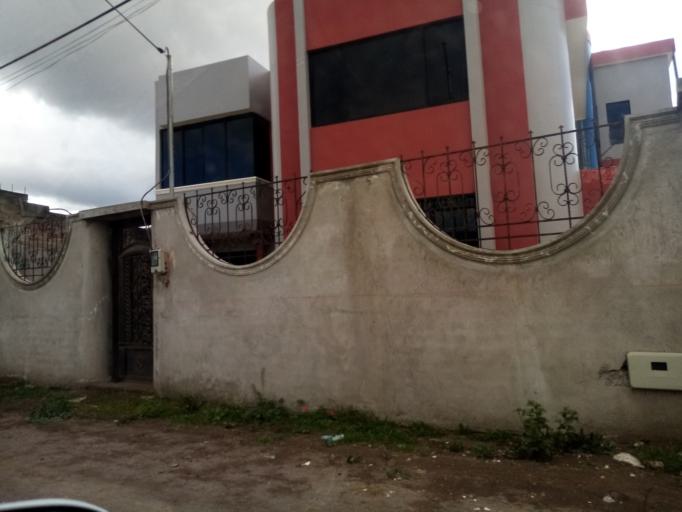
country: EC
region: Chimborazo
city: Riobamba
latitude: -1.6855
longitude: -78.6260
